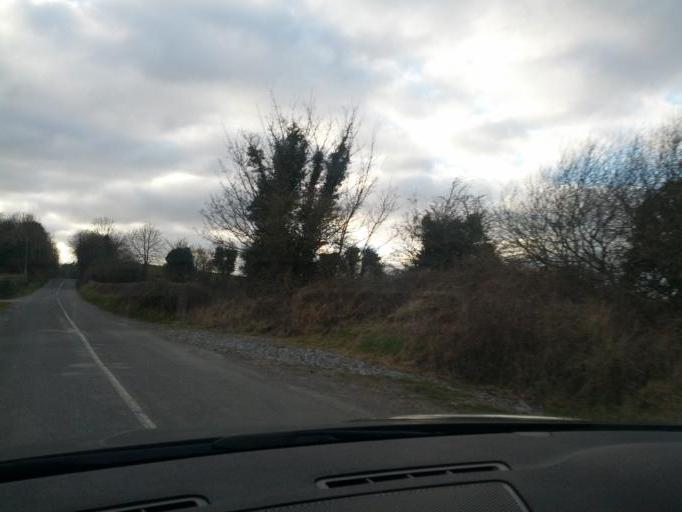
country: IE
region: Leinster
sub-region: An Iarmhi
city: Athlone
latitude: 53.3221
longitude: -7.9564
